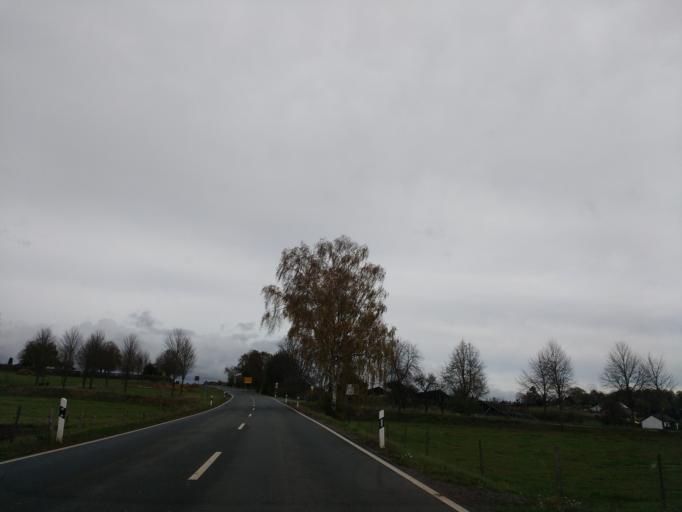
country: DE
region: Hesse
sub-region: Regierungsbezirk Kassel
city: Vohl
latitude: 51.2067
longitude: 8.9793
